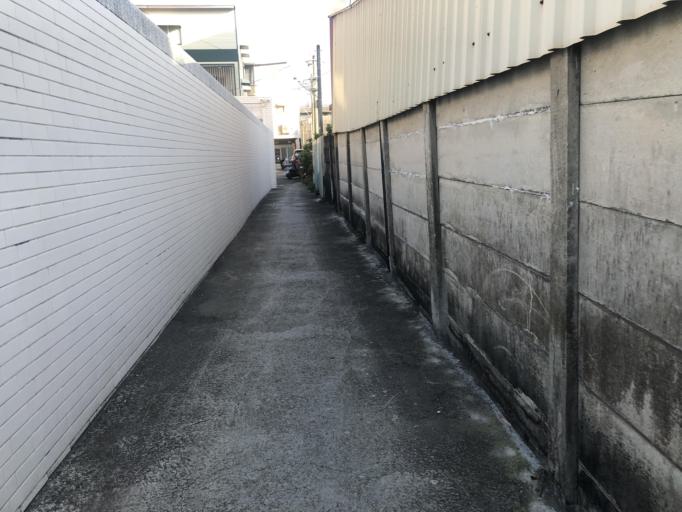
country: TW
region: Taiwan
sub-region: Tainan
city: Tainan
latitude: 23.0389
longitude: 120.1828
